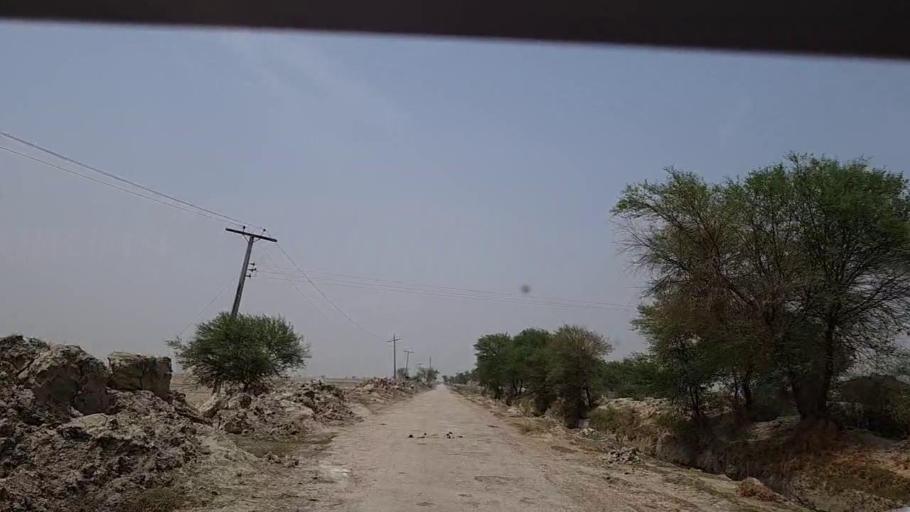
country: PK
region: Sindh
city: Khairpur Nathan Shah
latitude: 27.0450
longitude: 67.6189
